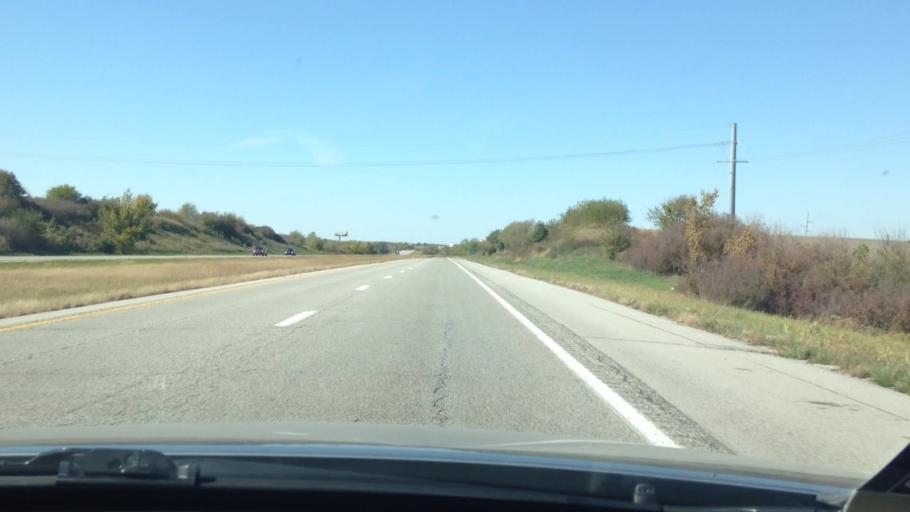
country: US
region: Missouri
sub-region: Platte County
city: Weatherby Lake
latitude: 39.3164
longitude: -94.6823
